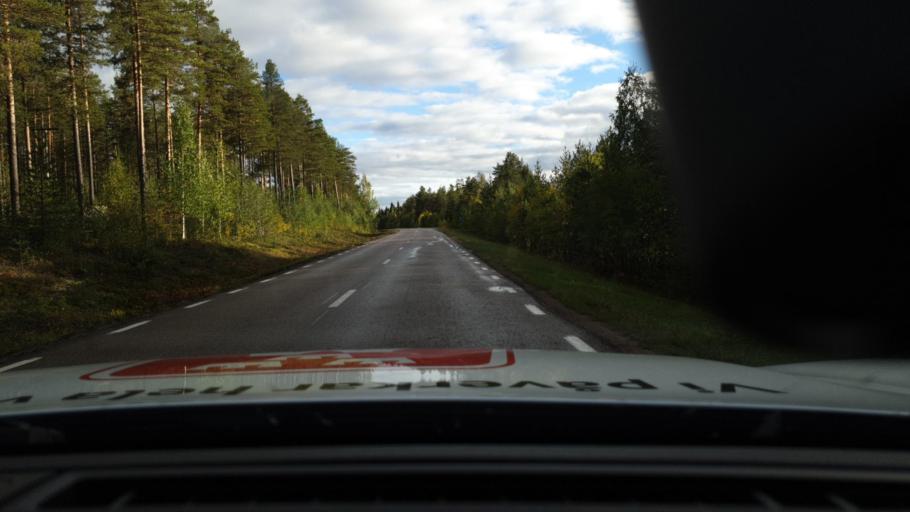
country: SE
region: Norrbotten
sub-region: Overkalix Kommun
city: OEverkalix
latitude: 66.6445
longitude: 22.7213
